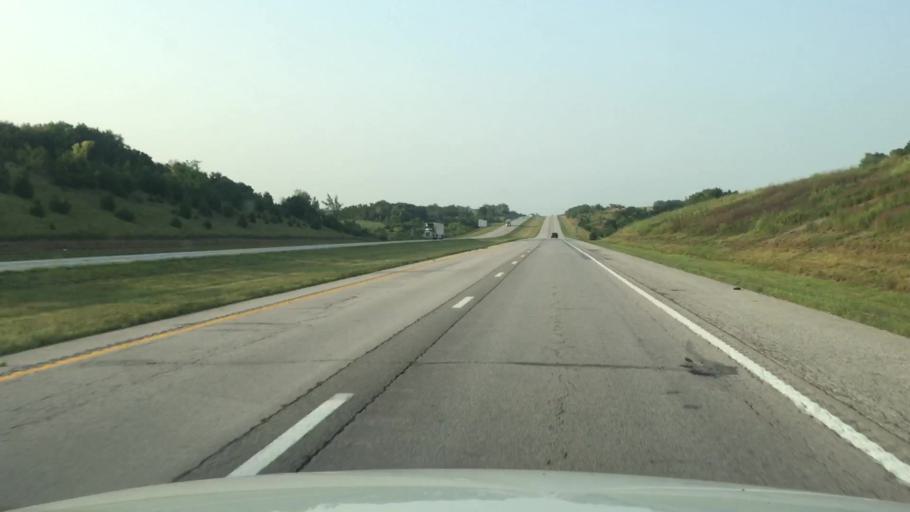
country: US
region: Missouri
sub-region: Harrison County
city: Bethany
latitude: 40.3867
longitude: -93.9993
